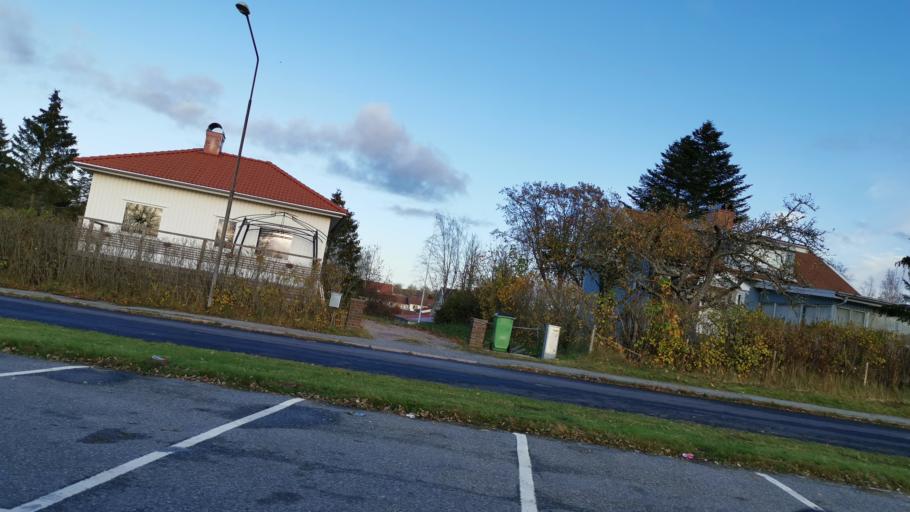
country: SE
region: Vaestra Goetaland
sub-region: Munkedals Kommun
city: Munkedal
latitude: 58.4729
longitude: 11.6658
